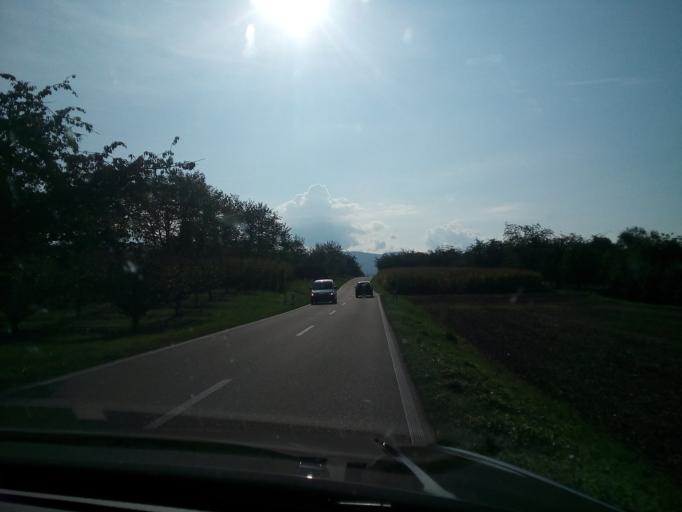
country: DE
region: Baden-Wuerttemberg
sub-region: Freiburg Region
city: Renchen
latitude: 48.5762
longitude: 8.0268
